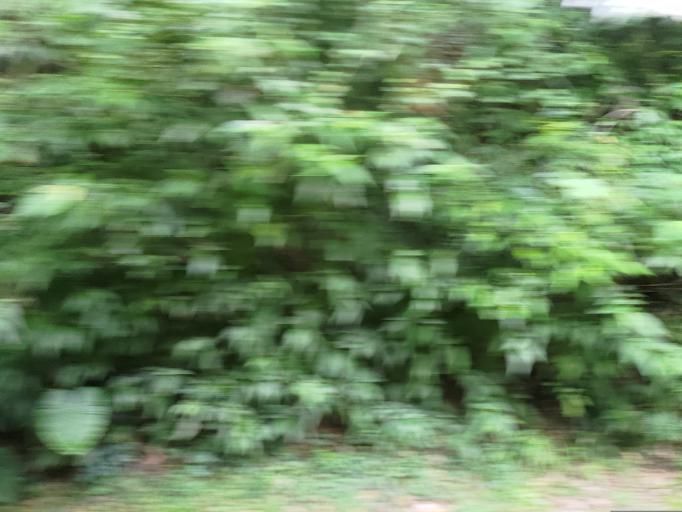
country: TW
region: Taiwan
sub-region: Hsinchu
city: Hsinchu
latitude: 24.6054
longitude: 121.0388
